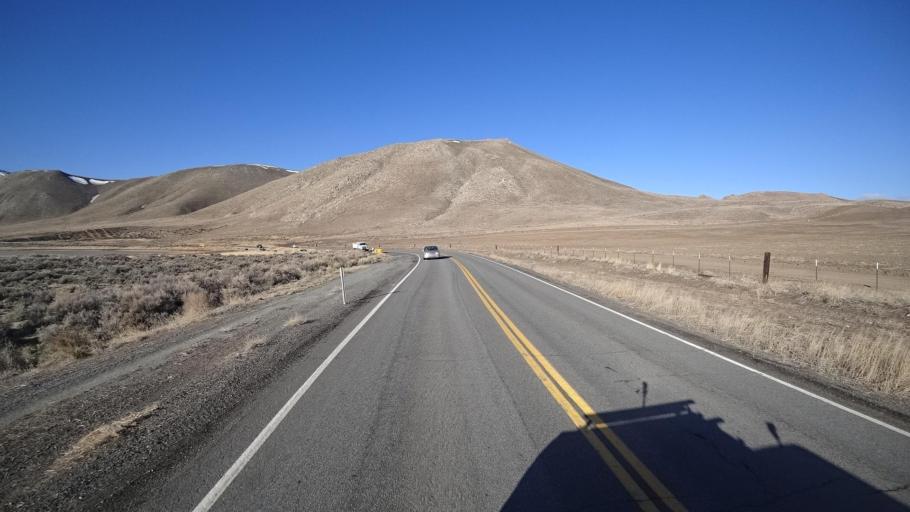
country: US
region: Nevada
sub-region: Washoe County
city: Cold Springs
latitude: 39.6522
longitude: -119.9249
